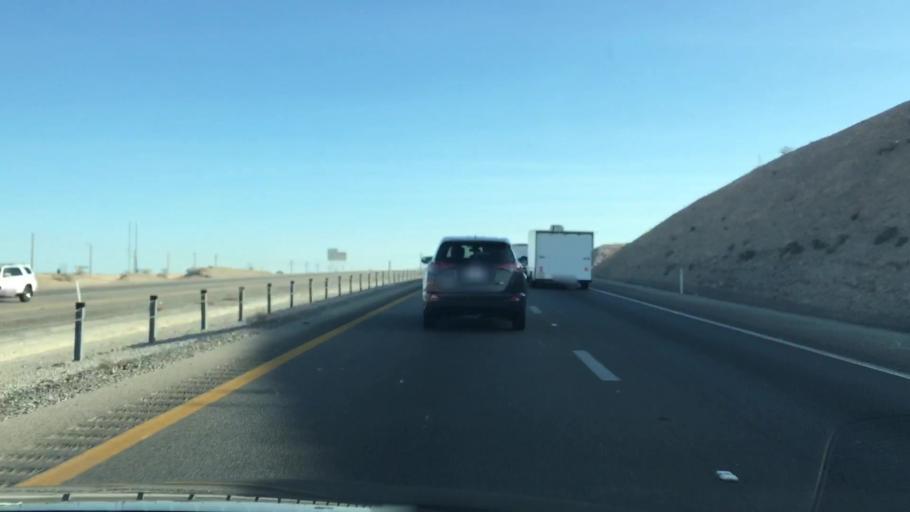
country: US
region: Nevada
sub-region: Clark County
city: Nellis Air Force Base
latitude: 36.3213
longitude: -114.9364
